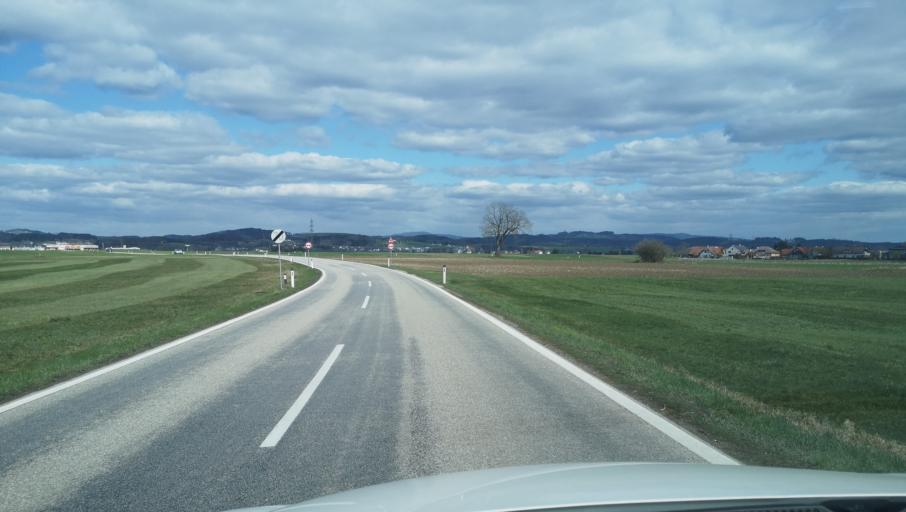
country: AT
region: Lower Austria
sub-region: Politischer Bezirk Amstetten
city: Euratsfeld
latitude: 48.1037
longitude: 14.9412
